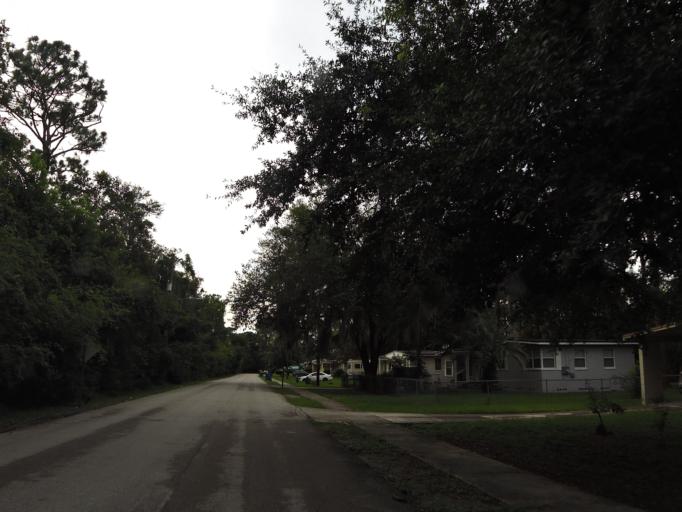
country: US
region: Florida
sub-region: Duval County
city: Jacksonville
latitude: 30.3959
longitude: -81.6964
